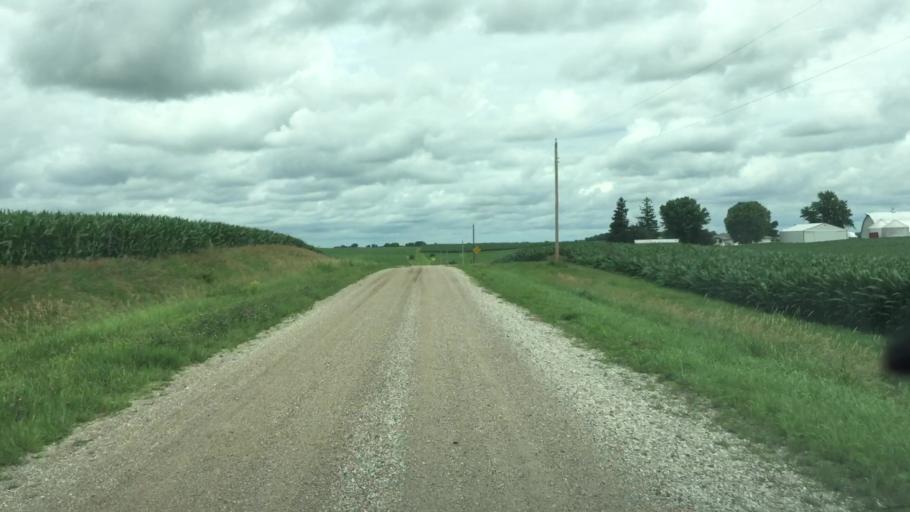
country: US
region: Iowa
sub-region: Jasper County
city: Monroe
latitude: 41.5774
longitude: -93.1208
